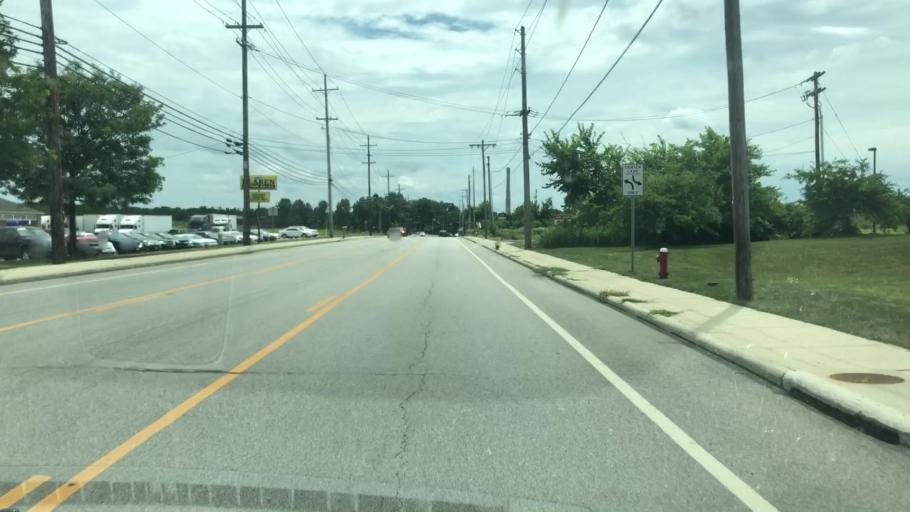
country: US
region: Ohio
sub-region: Summit County
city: Cuyahoga Falls
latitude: 41.1661
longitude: -81.5087
